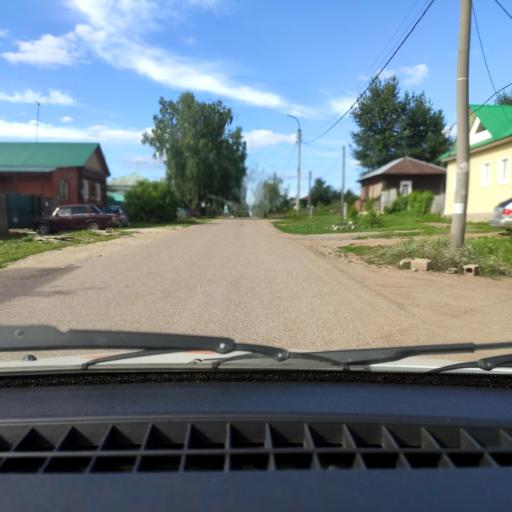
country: RU
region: Bashkortostan
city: Blagoveshchensk
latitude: 55.0269
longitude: 55.9804
